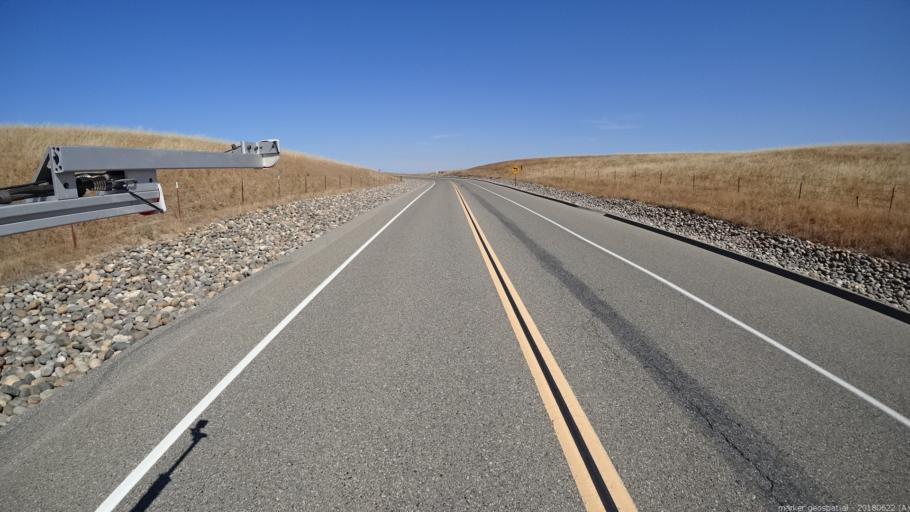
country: US
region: California
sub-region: Madera County
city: Bonadelle Ranchos-Madera Ranchos
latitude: 36.9256
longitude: -119.7716
